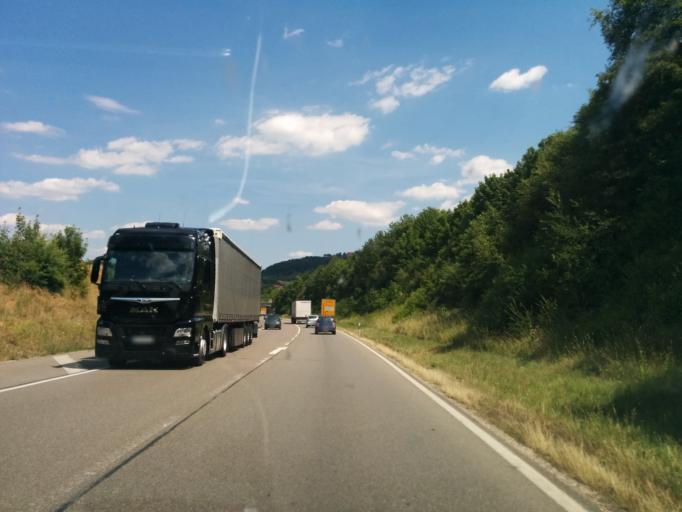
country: DE
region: Bavaria
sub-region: Regierungsbezirk Mittelfranken
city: Weissenburg in Bayern
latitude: 49.0218
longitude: 10.9768
